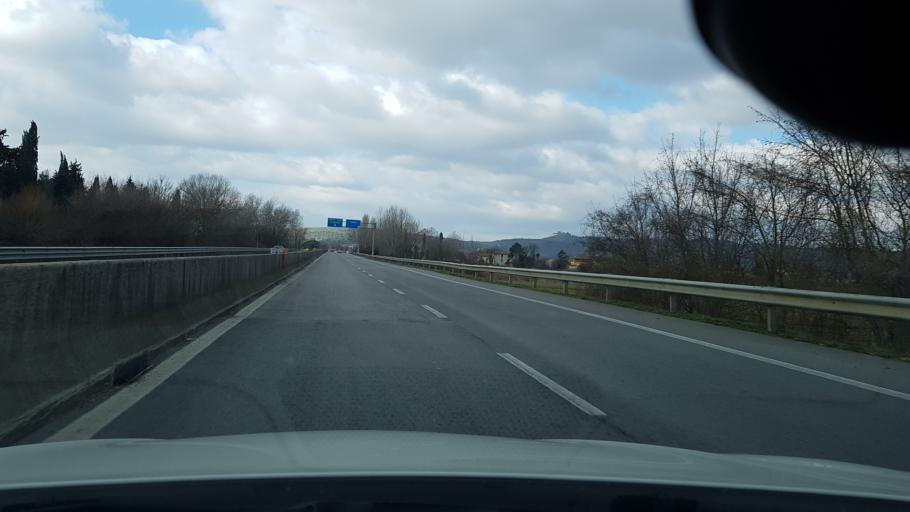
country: IT
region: Umbria
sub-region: Provincia di Perugia
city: Tuoro sul Trasimeno
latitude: 43.1977
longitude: 12.0825
